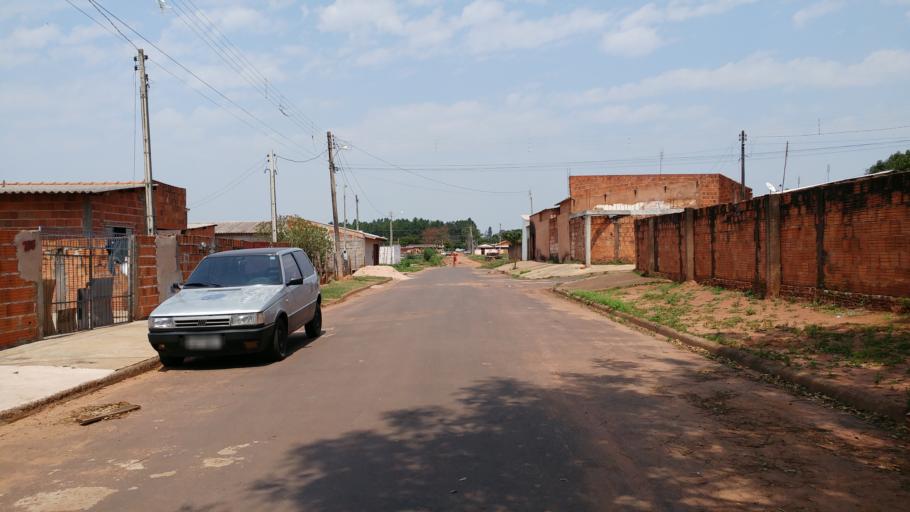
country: BR
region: Sao Paulo
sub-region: Paraguacu Paulista
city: Paraguacu Paulista
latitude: -22.4158
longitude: -50.5656
